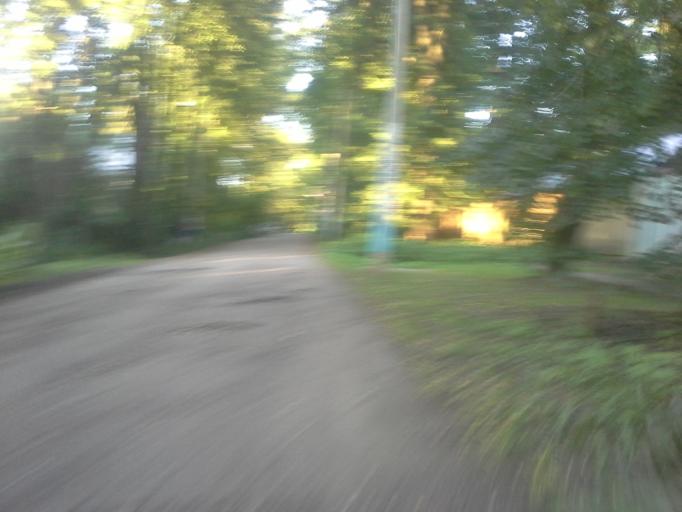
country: RU
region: Moscow
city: Novo-Peredelkino
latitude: 55.6483
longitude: 37.3241
